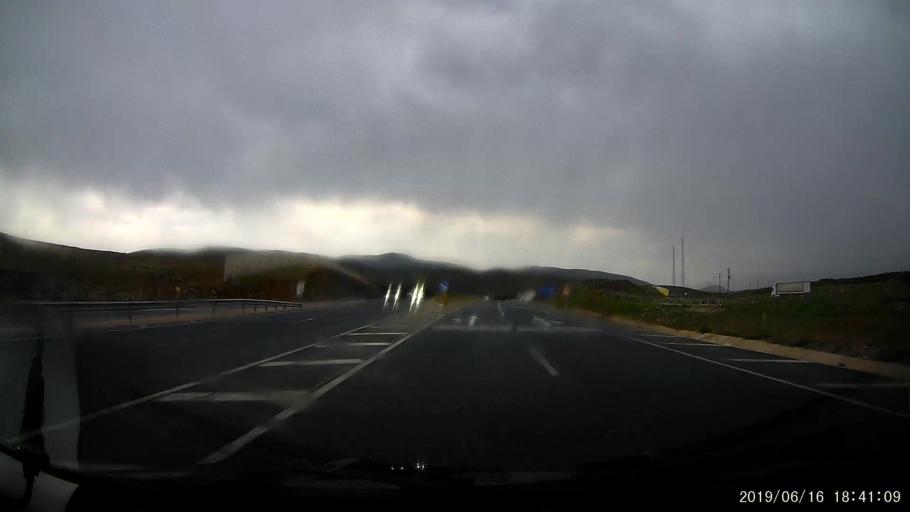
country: TR
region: Erzincan
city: Catalarmut
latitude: 39.8768
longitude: 39.1324
